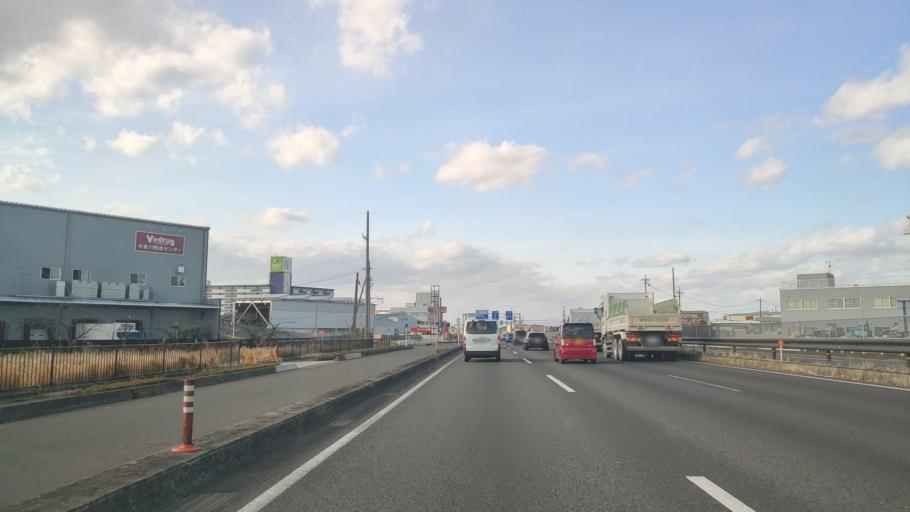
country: JP
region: Aichi
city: Kuroda
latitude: 35.3492
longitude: 136.7923
